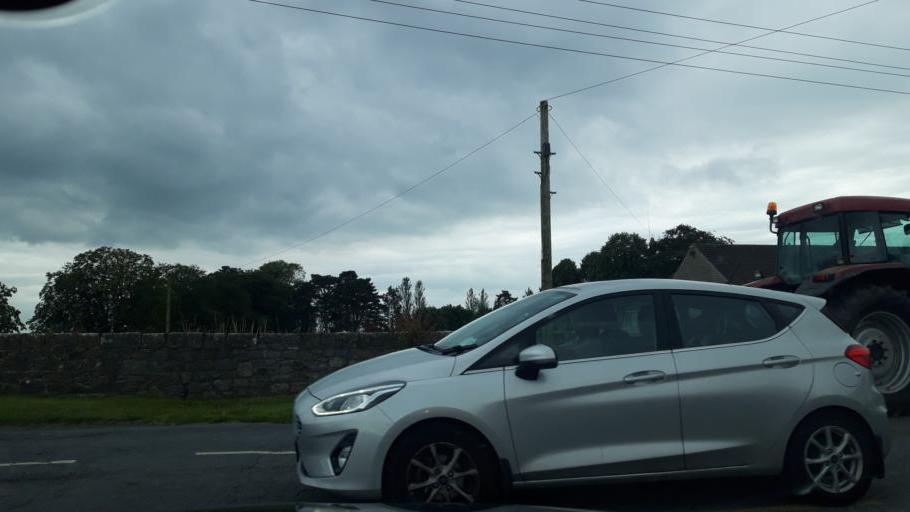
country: IE
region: Leinster
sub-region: Kilkenny
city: Ballyragget
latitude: 52.7907
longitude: -7.3302
